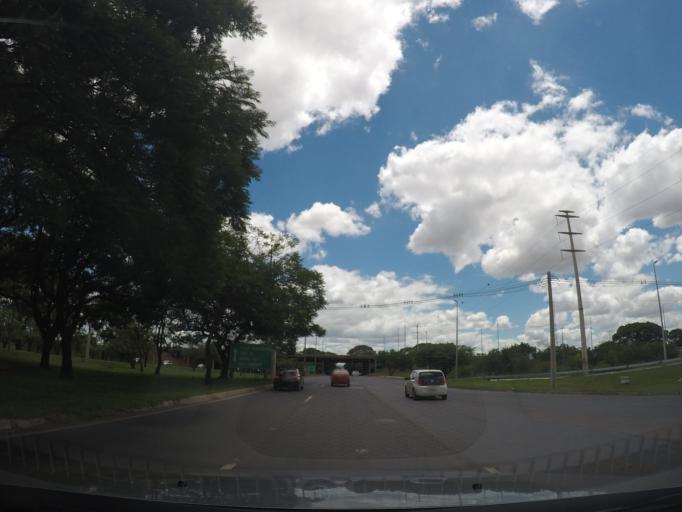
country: BR
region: Federal District
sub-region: Brasilia
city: Brasilia
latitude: -15.8086
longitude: -47.9484
